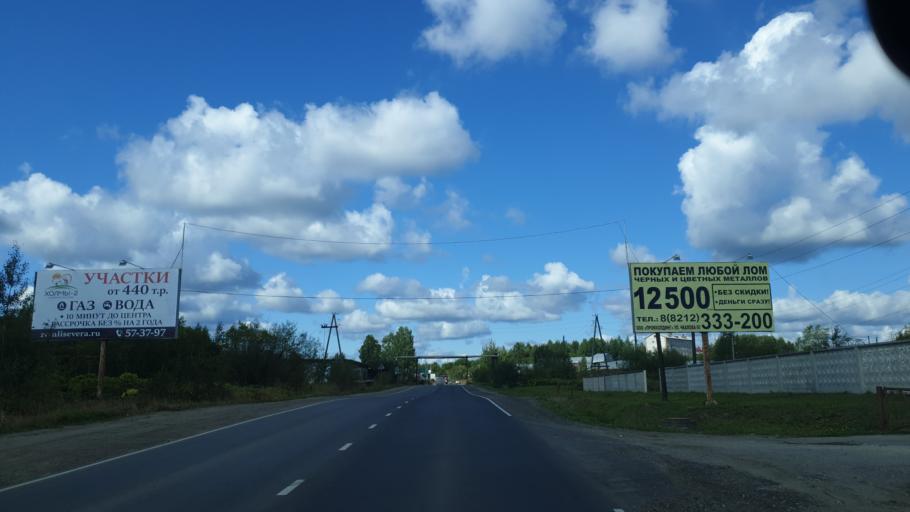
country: RU
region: Komi Republic
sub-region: Syktyvdinskiy Rayon
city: Syktyvkar
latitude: 61.6401
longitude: 50.7979
